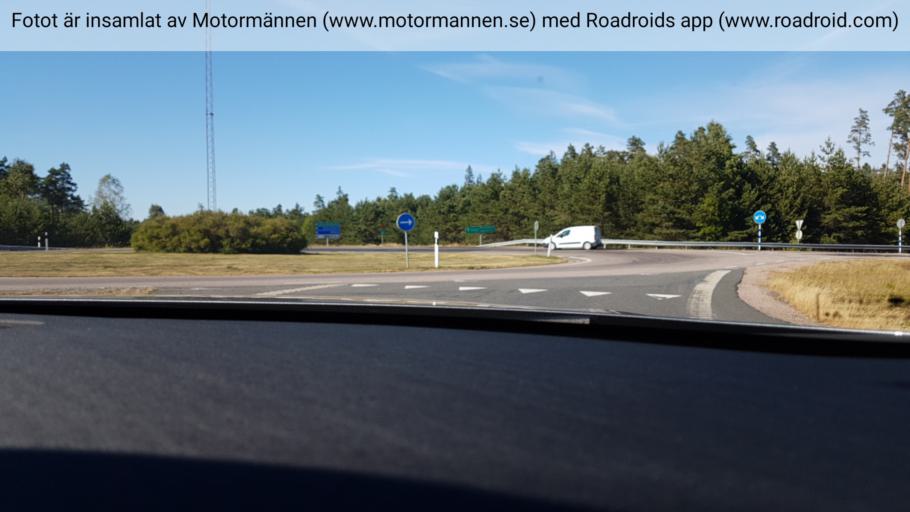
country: SE
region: Joenkoeping
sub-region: Vaggeryds Kommun
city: Skillingaryd
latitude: 57.3453
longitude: 14.1051
